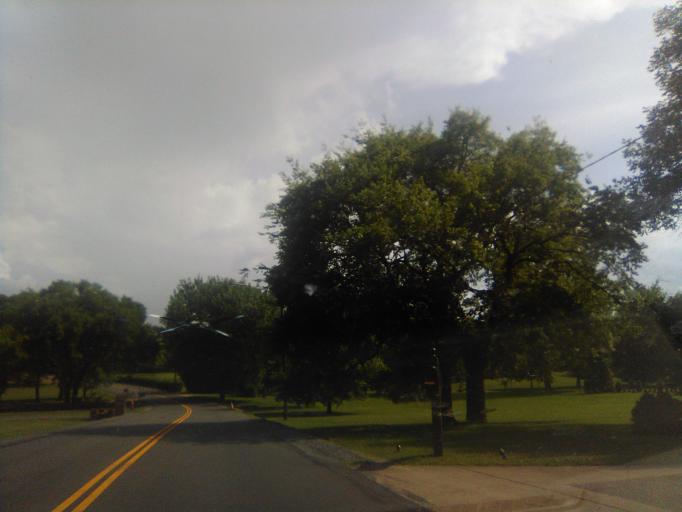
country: US
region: Tennessee
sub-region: Davidson County
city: Belle Meade
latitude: 36.0974
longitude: -86.8834
